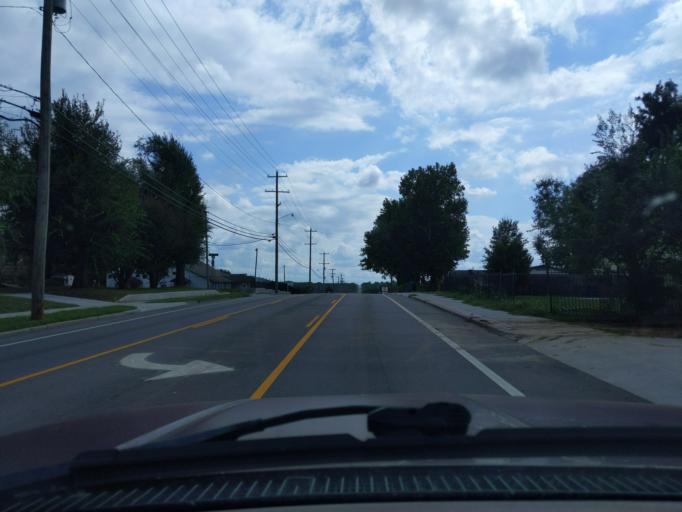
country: US
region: Oklahoma
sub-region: Tulsa County
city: Oakhurst
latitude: 36.0958
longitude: -96.0117
